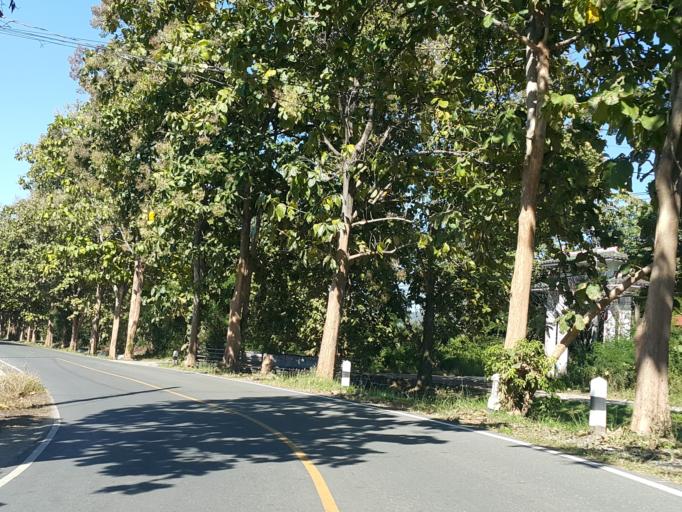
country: TH
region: Chiang Mai
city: San Sai
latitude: 18.8898
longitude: 99.1418
